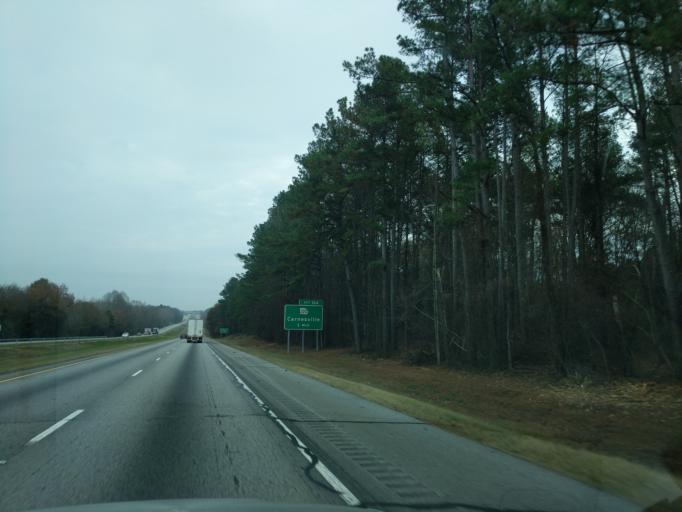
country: US
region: Georgia
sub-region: Franklin County
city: Carnesville
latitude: 34.3664
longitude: -83.2857
